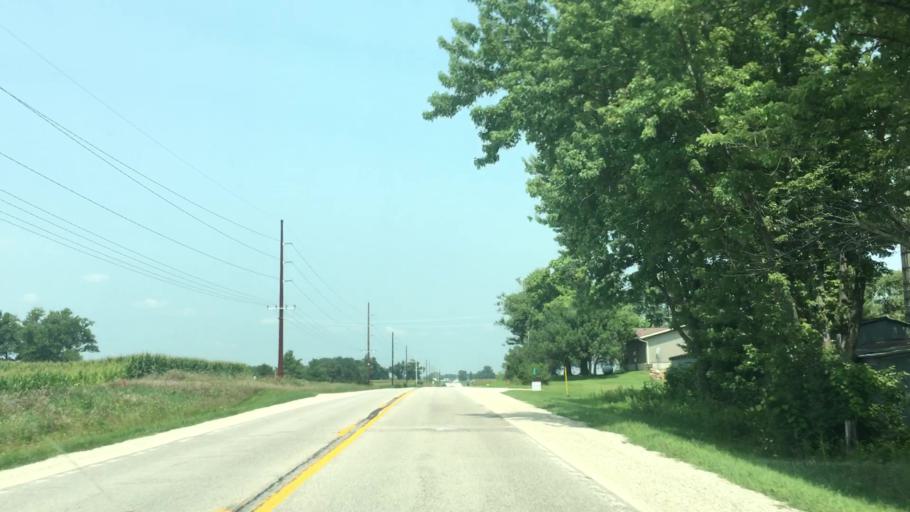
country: US
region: Iowa
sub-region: Buchanan County
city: Independence
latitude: 42.3955
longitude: -91.8899
